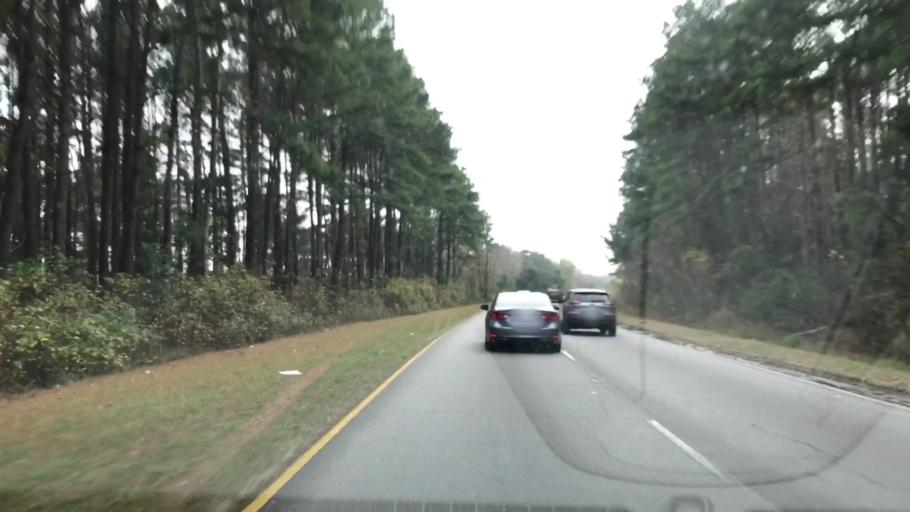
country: US
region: South Carolina
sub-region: Berkeley County
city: Goose Creek
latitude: 32.9481
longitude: -80.0439
